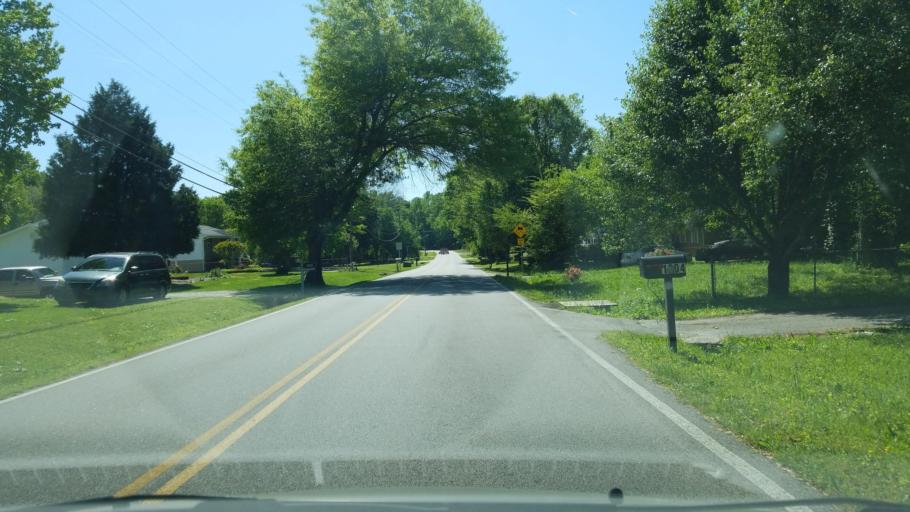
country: US
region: Tennessee
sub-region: Hamilton County
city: Middle Valley
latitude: 35.1751
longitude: -85.2147
